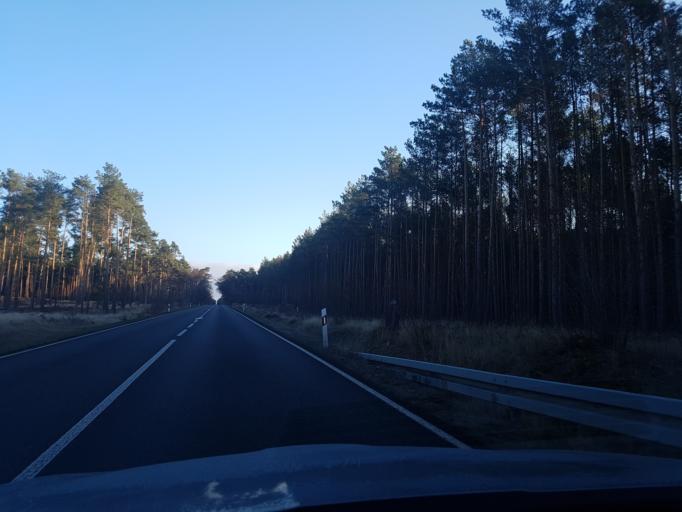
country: DE
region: Brandenburg
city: Hohenbucko
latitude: 51.7474
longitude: 13.4465
